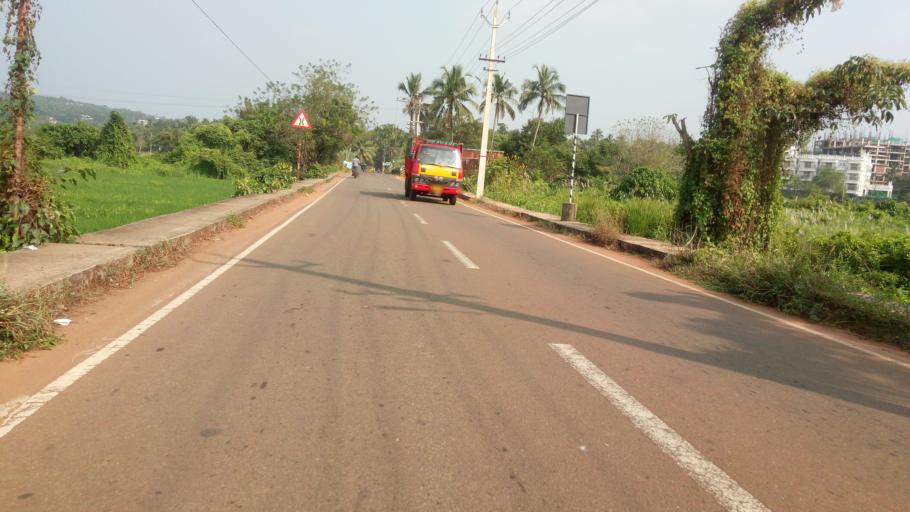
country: IN
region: Kerala
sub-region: Malappuram
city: Malappuram
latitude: 10.9940
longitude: 76.0119
